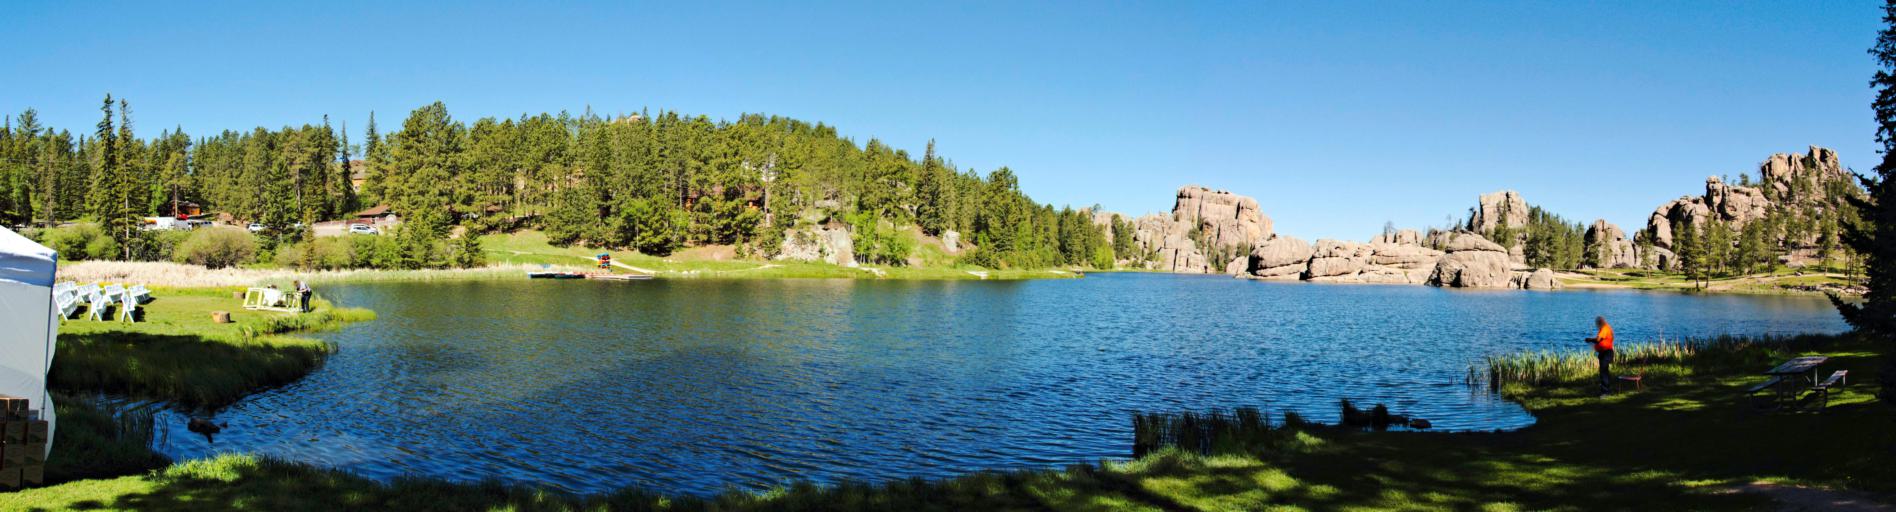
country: US
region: South Dakota
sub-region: Custer County
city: Custer
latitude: 43.8442
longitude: -103.5613
